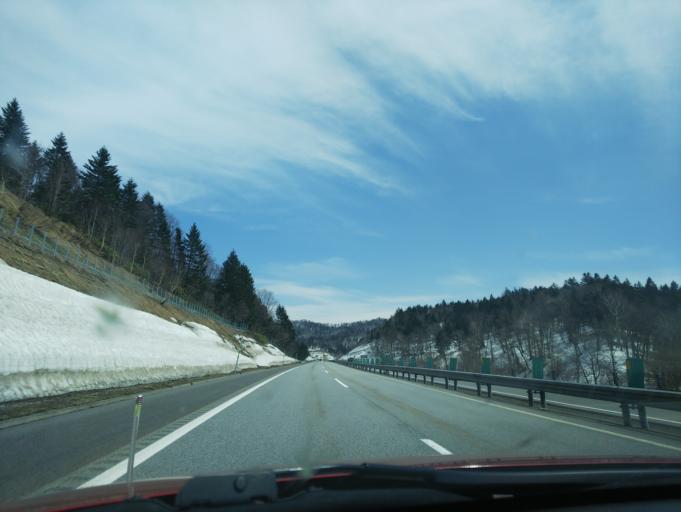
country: JP
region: Hokkaido
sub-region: Asahikawa-shi
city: Asahikawa
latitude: 43.7807
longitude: 142.2006
